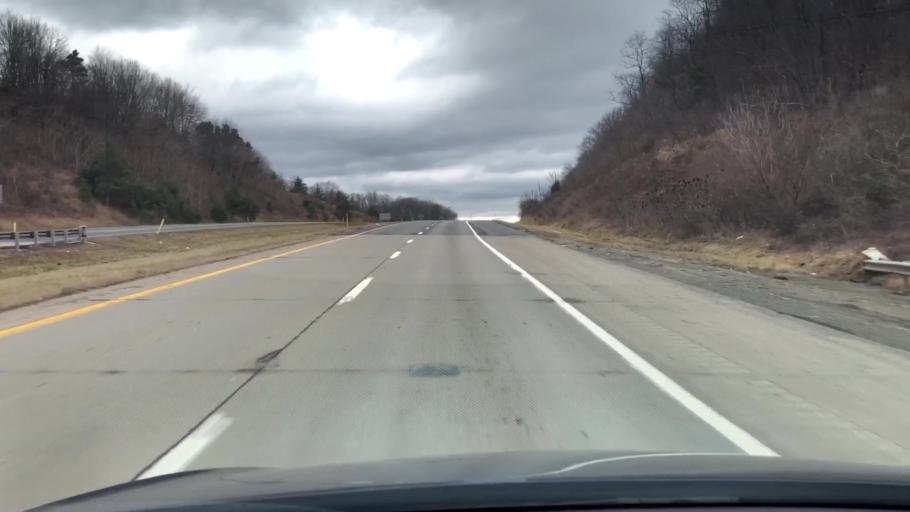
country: US
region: Pennsylvania
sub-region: Westmoreland County
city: New Stanton
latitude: 40.2139
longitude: -79.5907
